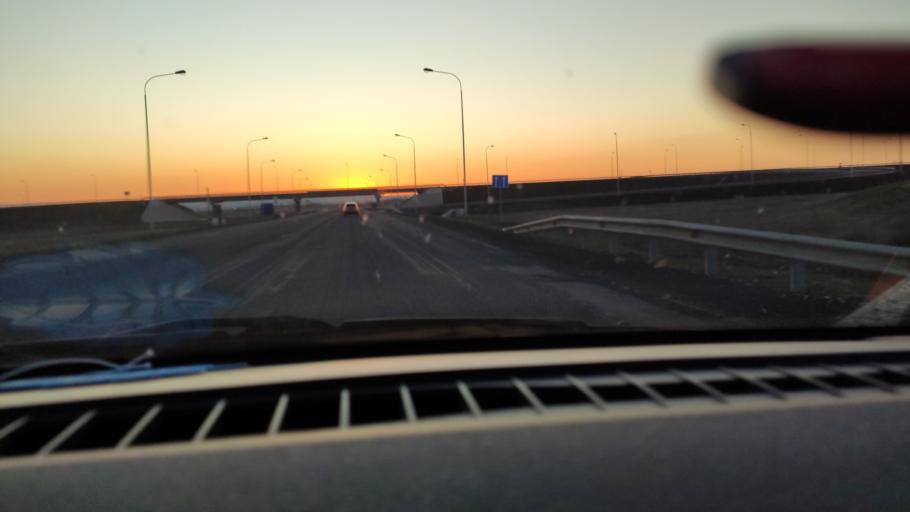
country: RU
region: Saratov
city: Yelshanka
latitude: 51.7961
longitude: 46.1720
